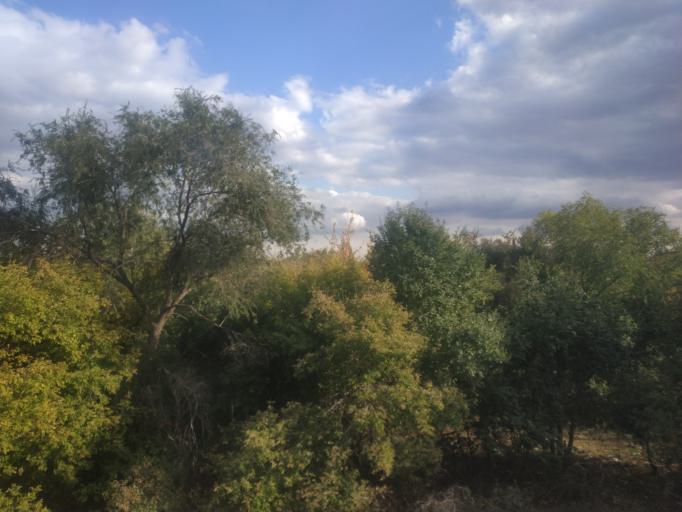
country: RU
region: Volgograd
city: Krasnoslobodsk
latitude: 48.5074
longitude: 44.5519
